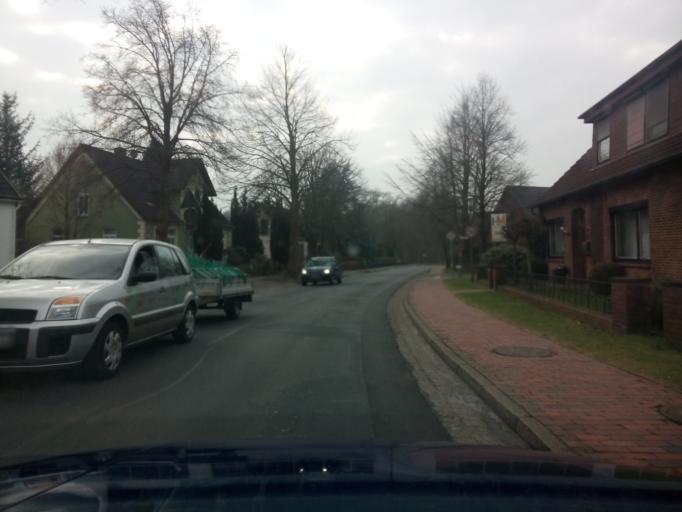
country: DE
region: Lower Saxony
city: Lintig
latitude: 53.6198
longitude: 8.8354
